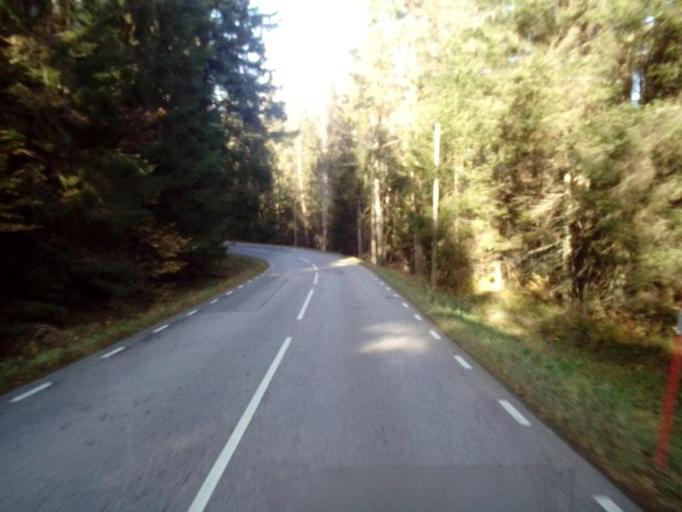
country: SE
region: Kalmar
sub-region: Vasterviks Kommun
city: Ankarsrum
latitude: 57.7332
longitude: 16.0887
